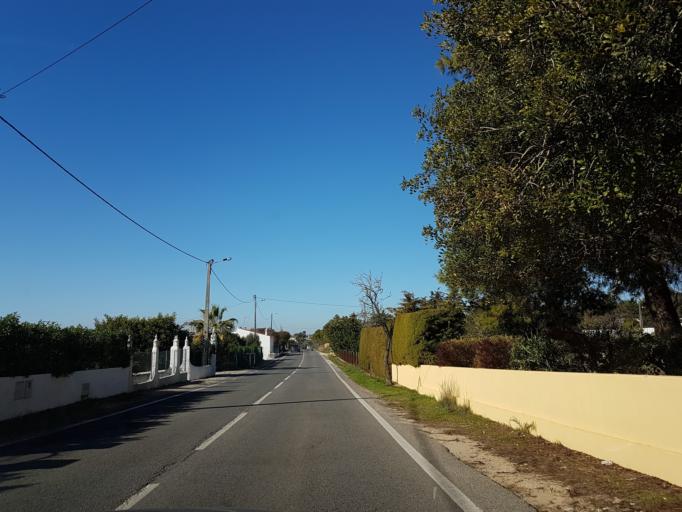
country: PT
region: Faro
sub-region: Lagoa
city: Carvoeiro
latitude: 37.1112
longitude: -8.4470
